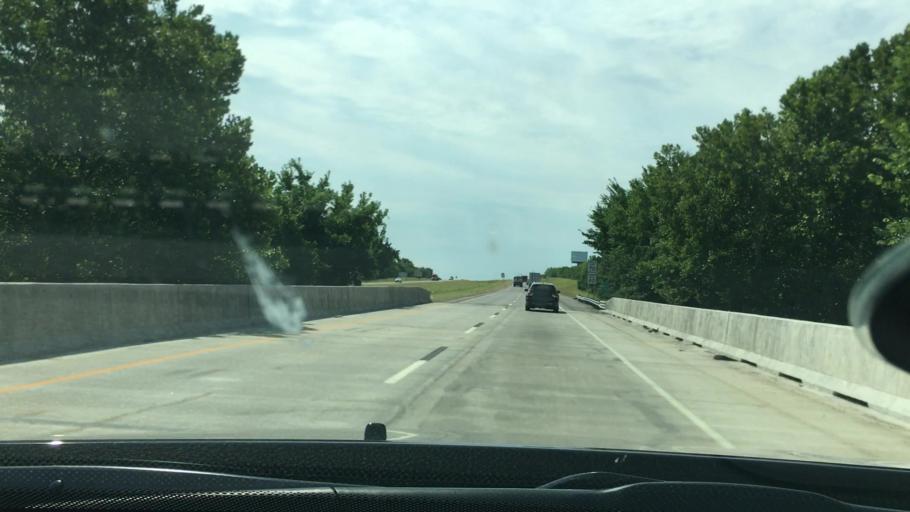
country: US
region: Oklahoma
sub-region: Murray County
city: Davis
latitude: 34.4988
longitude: -97.1694
